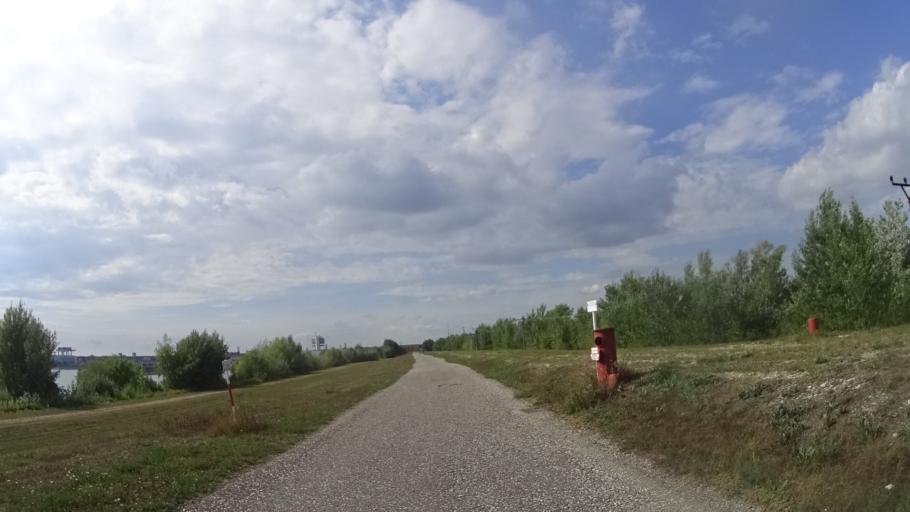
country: SK
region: Trnavsky
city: Gabcikovo
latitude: 47.8757
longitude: 17.5519
